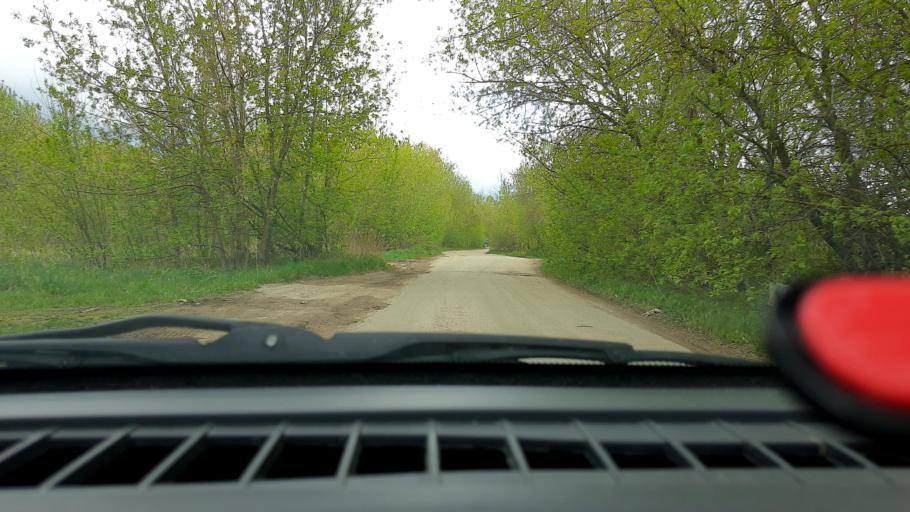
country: RU
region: Nizjnij Novgorod
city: Neklyudovo
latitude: 56.3871
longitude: 43.8413
